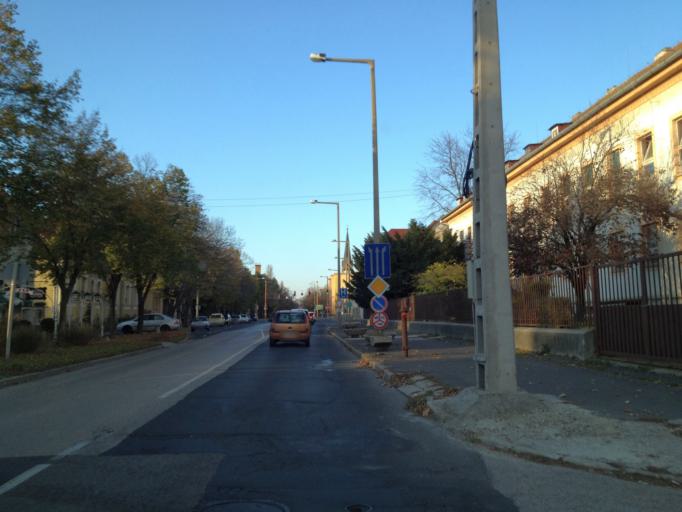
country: HU
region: Gyor-Moson-Sopron
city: Gyor
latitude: 47.6735
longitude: 17.6413
